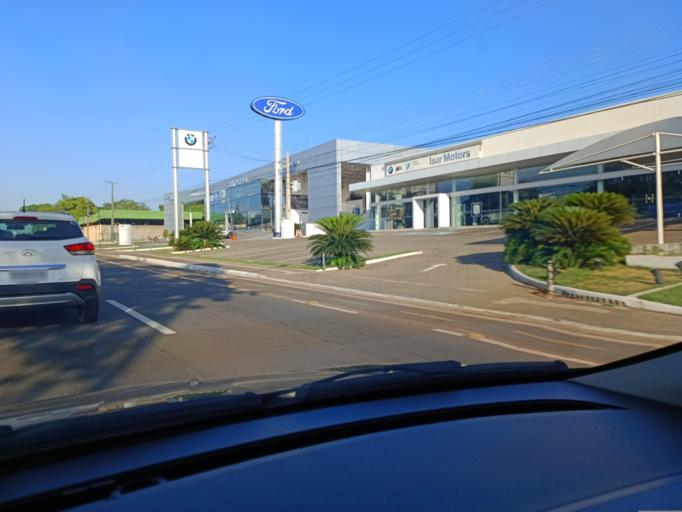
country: BR
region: Piaui
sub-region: Teresina
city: Teresina
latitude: -5.0810
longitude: -42.7612
